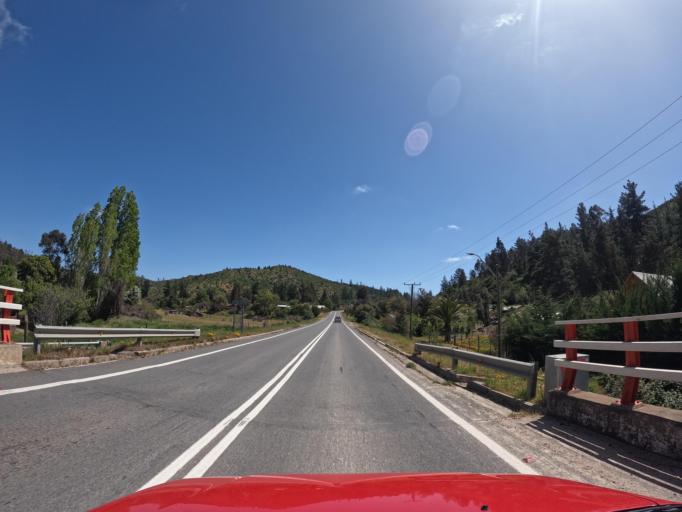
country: CL
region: O'Higgins
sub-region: Provincia de Colchagua
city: Santa Cruz
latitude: -34.6892
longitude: -71.7828
